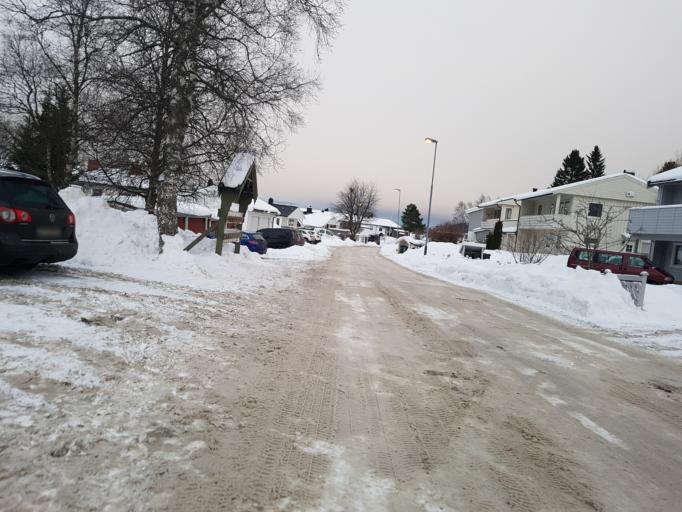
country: NO
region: Sor-Trondelag
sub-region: Trondheim
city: Trondheim
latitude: 63.3719
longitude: 10.3874
